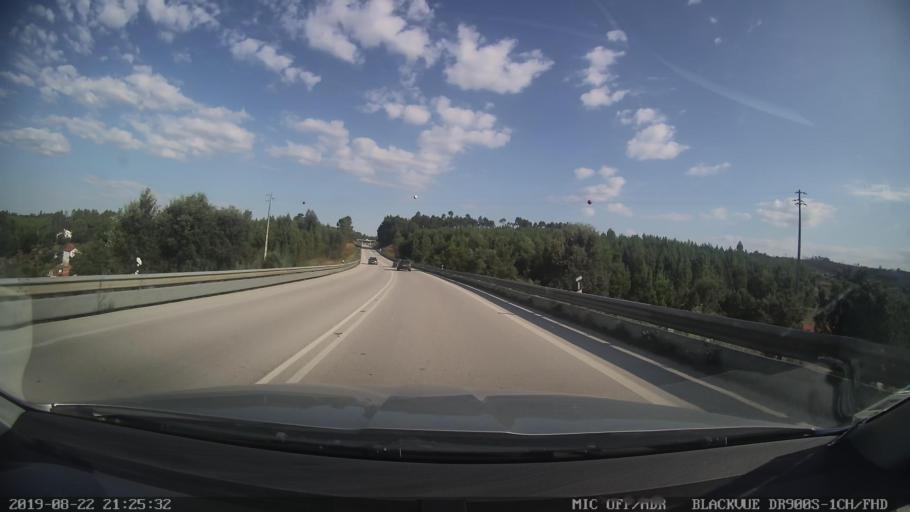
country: PT
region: Castelo Branco
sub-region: Serta
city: Serta
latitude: 39.8556
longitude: -8.1247
